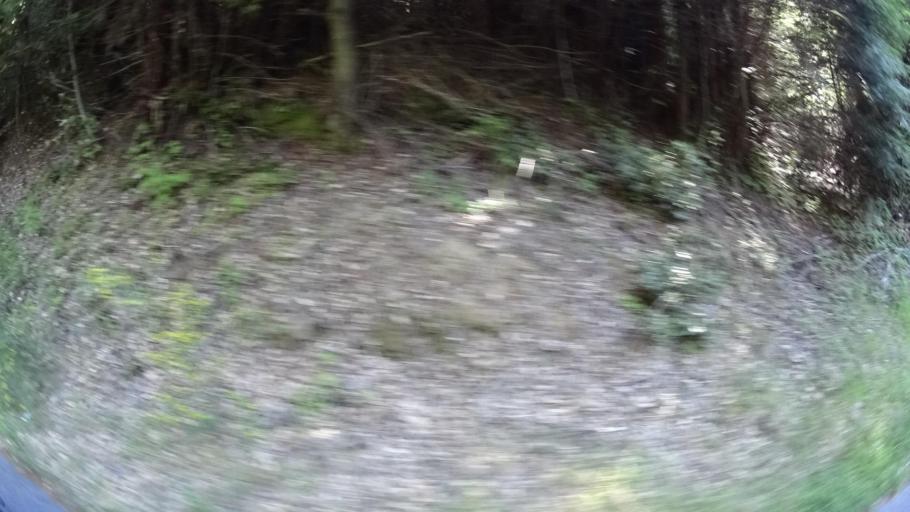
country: US
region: California
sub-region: Humboldt County
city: Rio Dell
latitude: 40.4595
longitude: -124.0031
